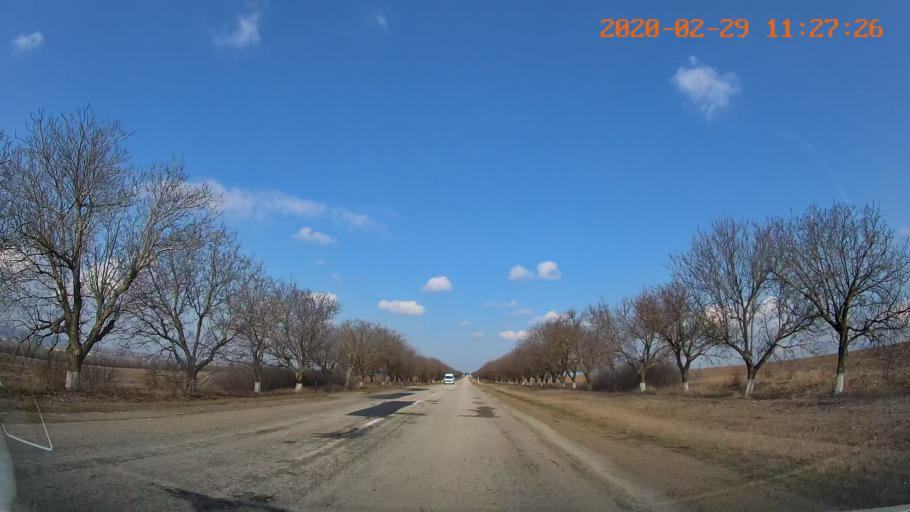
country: MD
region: Telenesti
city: Cocieri
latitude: 47.4682
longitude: 29.1425
